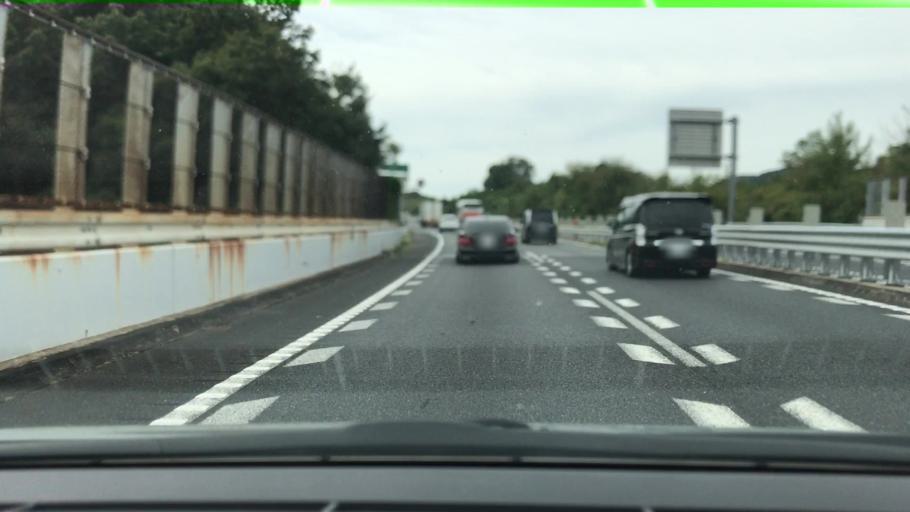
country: JP
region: Hyogo
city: Aioi
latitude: 34.8227
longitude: 134.4628
